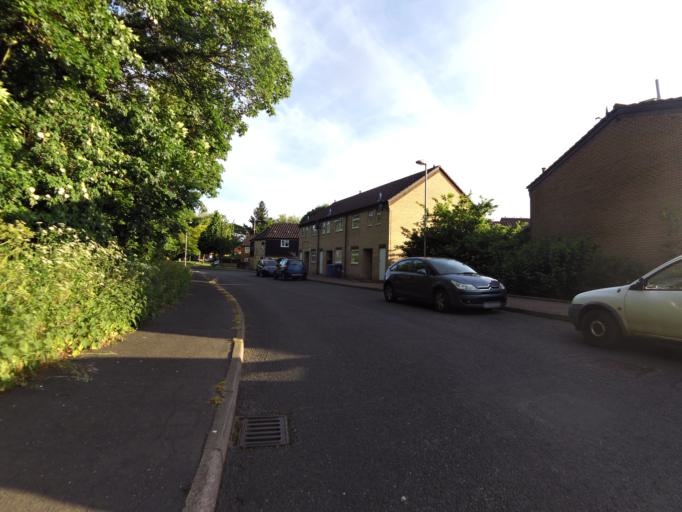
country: GB
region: England
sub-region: Norfolk
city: Norwich
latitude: 52.6571
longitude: 1.2904
